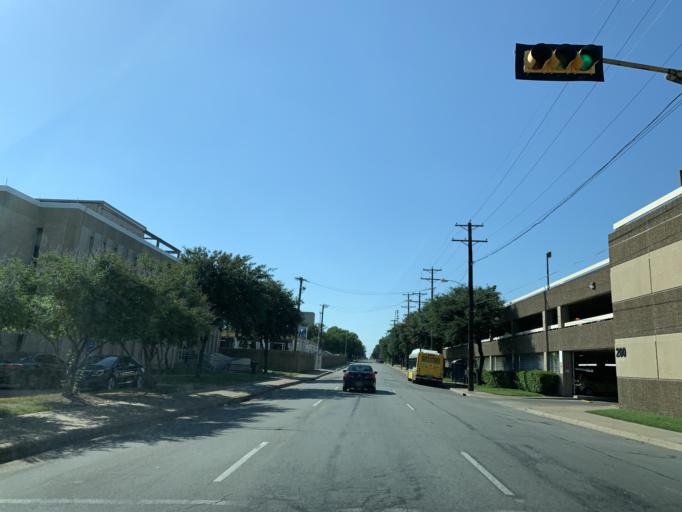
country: US
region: Texas
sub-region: Dallas County
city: Dallas
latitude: 32.7908
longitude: -96.7699
